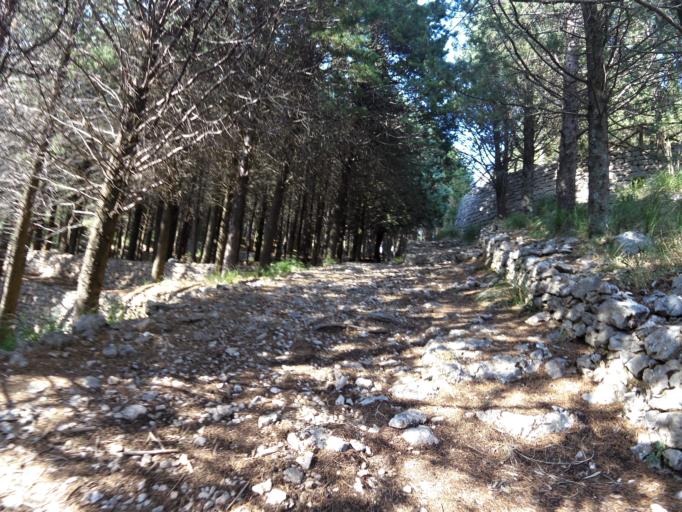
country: IT
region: Calabria
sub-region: Provincia di Reggio Calabria
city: Pazzano
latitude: 38.4686
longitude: 16.4484
